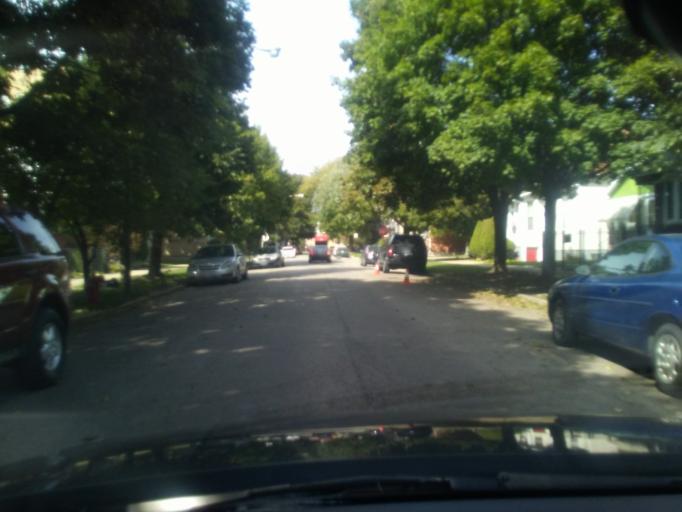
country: US
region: Illinois
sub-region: Cook County
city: Lincolnwood
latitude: 41.9352
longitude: -87.6953
